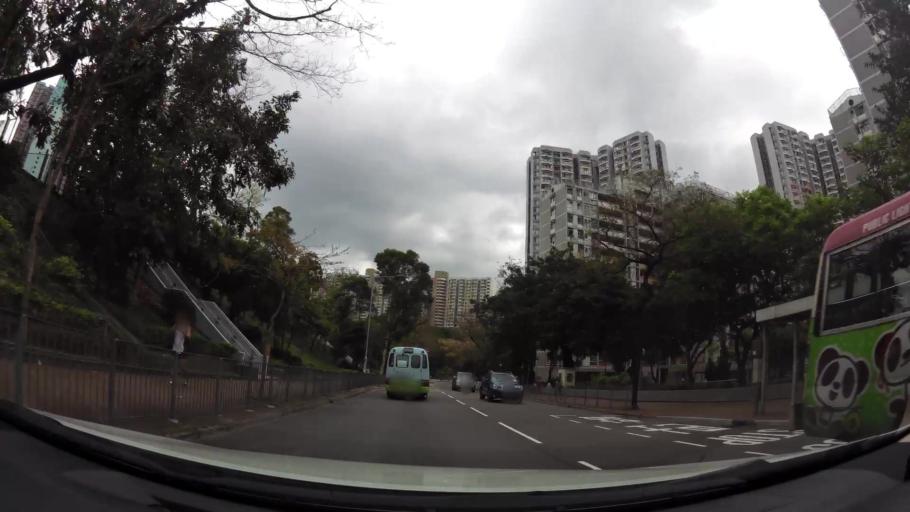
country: HK
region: Wong Tai Sin
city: Wong Tai Sin
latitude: 22.3354
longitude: 114.1913
